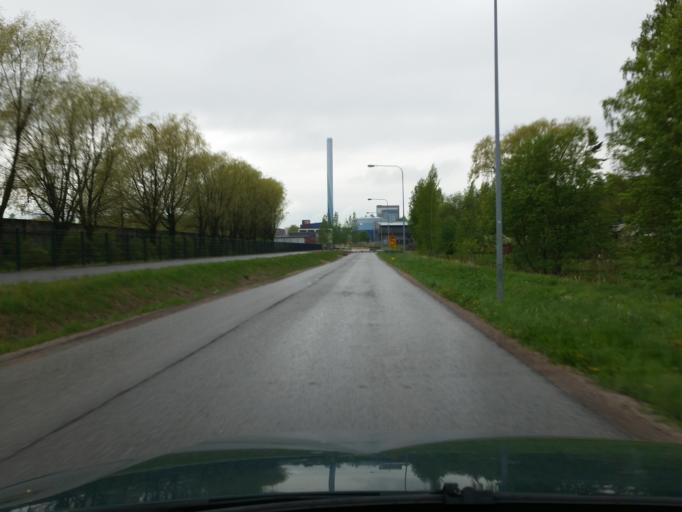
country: FI
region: Uusimaa
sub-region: Helsinki
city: Teekkarikylae
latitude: 60.2178
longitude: 24.8413
